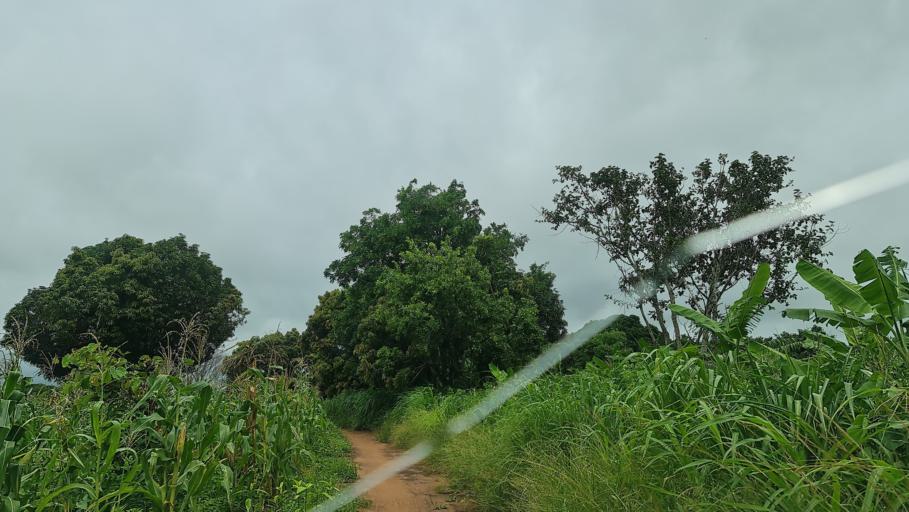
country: MW
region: Southern Region
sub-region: Nsanje District
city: Nsanje
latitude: -17.3836
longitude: 35.7778
